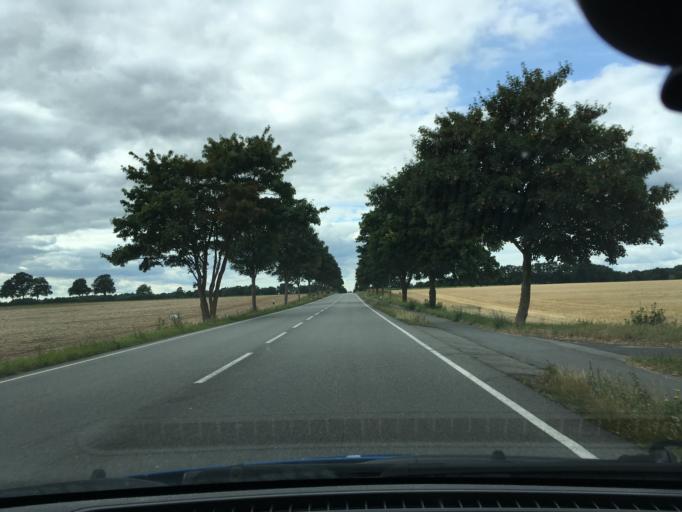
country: DE
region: Lower Saxony
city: Neu Wulmstorf
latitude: 53.4374
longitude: 9.7689
